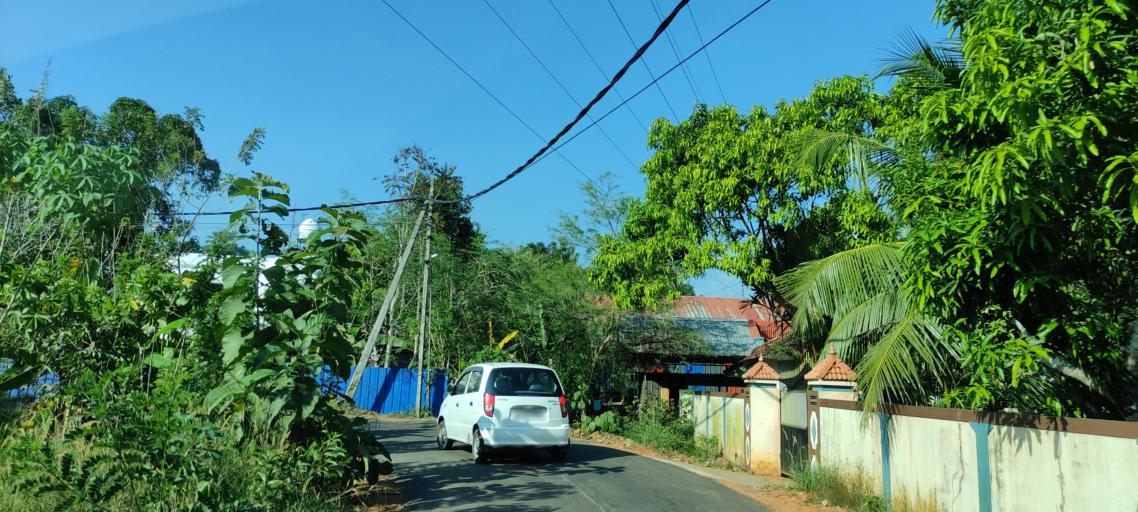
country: IN
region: Kerala
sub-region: Alappuzha
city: Shertallai
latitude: 9.6542
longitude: 76.3489
